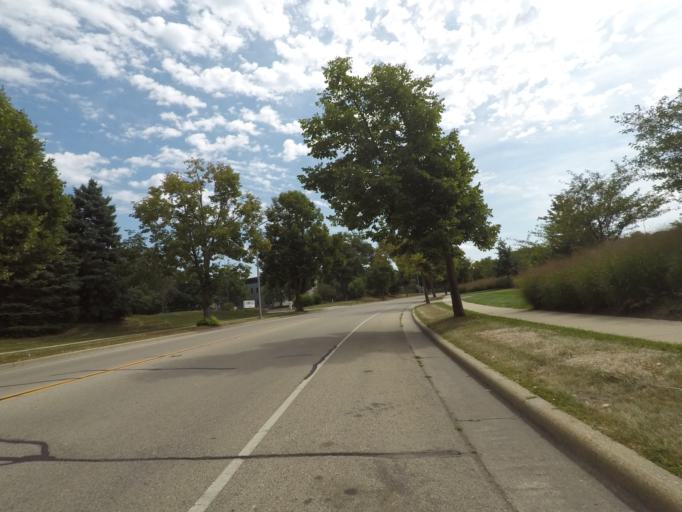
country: US
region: Wisconsin
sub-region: Dane County
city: Middleton
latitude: 43.0779
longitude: -89.5318
